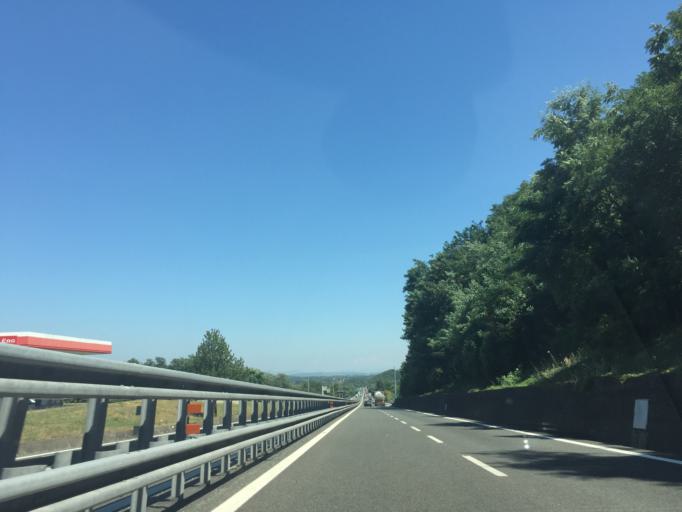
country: IT
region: Tuscany
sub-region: Province of Pisa
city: Filettole
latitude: 43.8535
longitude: 10.4067
